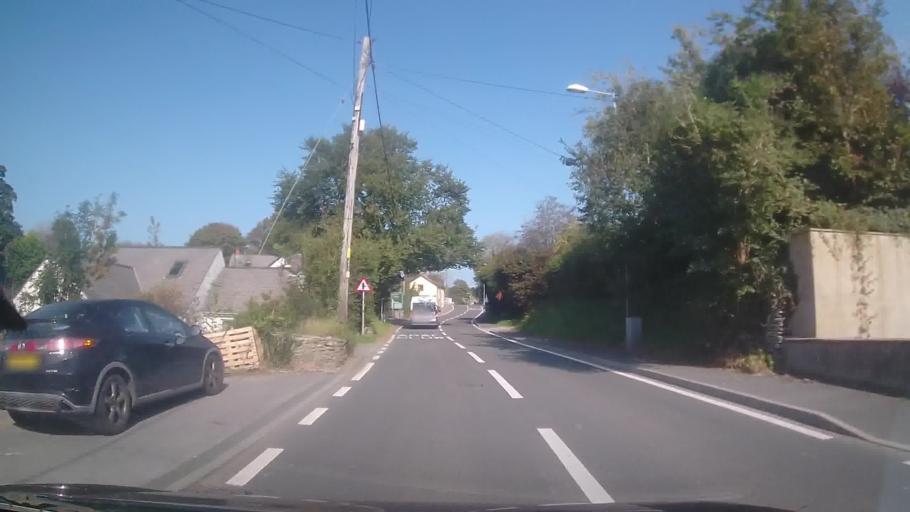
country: GB
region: Wales
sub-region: Pembrokeshire
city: Crymych
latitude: 52.0130
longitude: -4.7110
